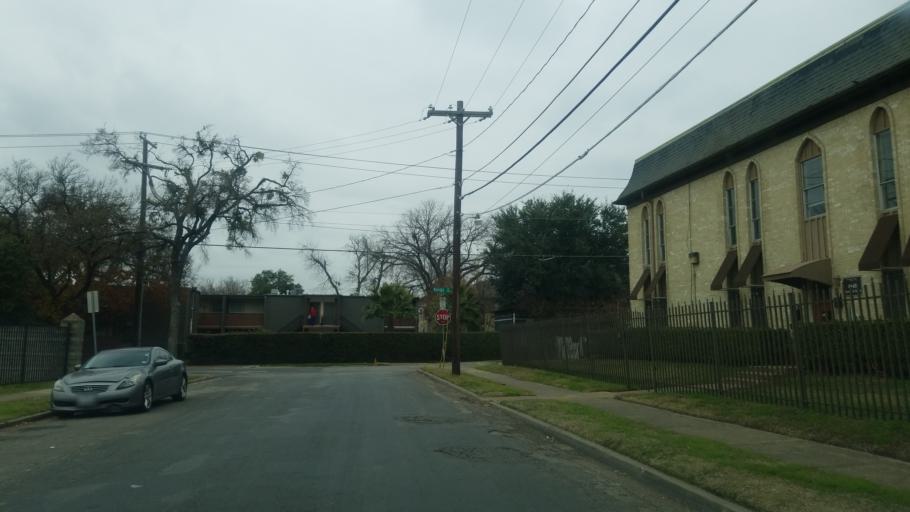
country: US
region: Texas
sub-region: Dallas County
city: Highland Park
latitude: 32.8167
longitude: -96.8213
